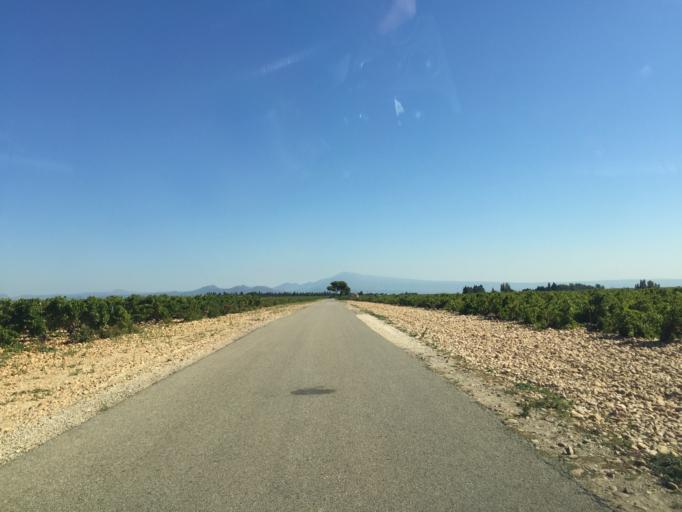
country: FR
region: Provence-Alpes-Cote d'Azur
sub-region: Departement du Vaucluse
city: Chateauneuf-du-Pape
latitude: 44.0818
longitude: 4.8136
